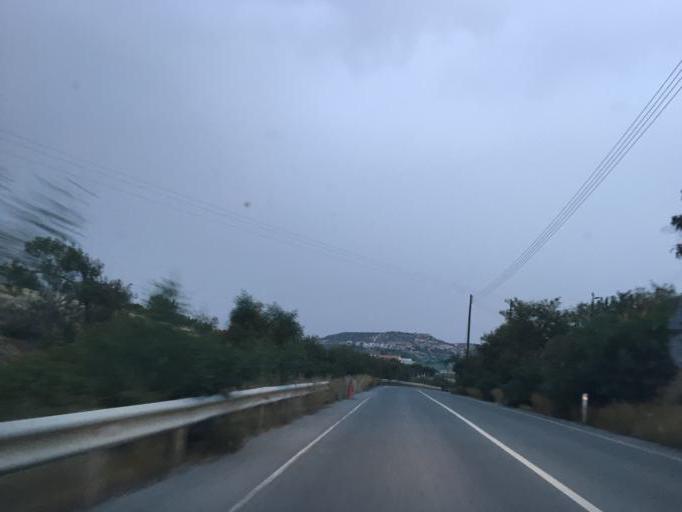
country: CY
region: Limassol
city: Parekklisha
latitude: 34.7604
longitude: 33.1597
